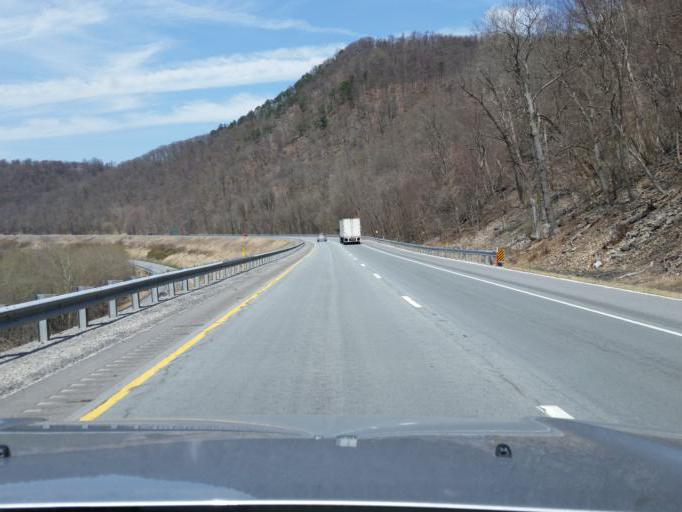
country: US
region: Pennsylvania
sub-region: Perry County
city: Duncannon
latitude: 40.4689
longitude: -77.0308
